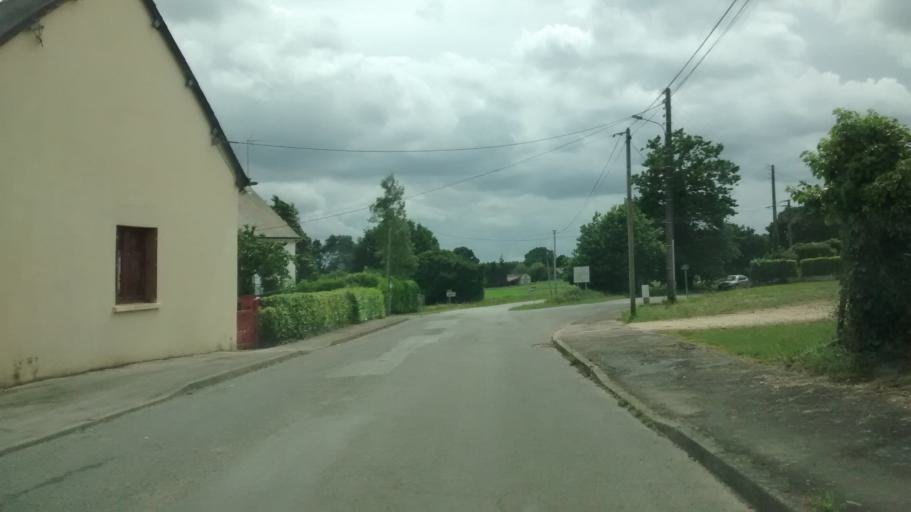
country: FR
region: Brittany
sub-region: Departement du Morbihan
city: Ruffiac
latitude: 47.8353
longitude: -2.2238
